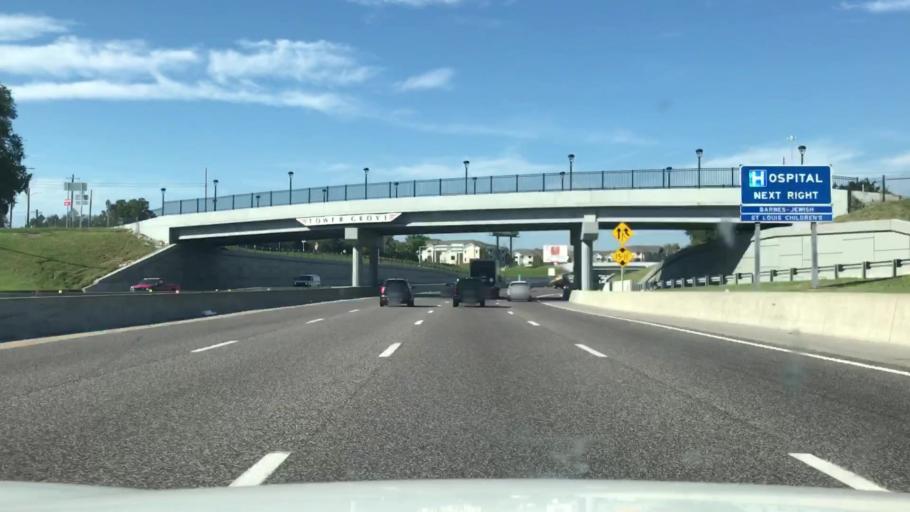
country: US
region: Missouri
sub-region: City of Saint Louis
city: St. Louis
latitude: 38.6312
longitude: -90.2539
